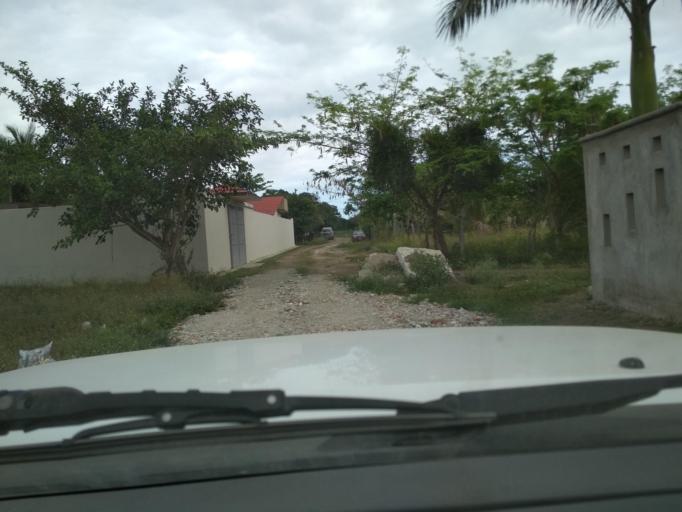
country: MX
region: Veracruz
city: El Tejar
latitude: 19.0727
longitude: -96.1477
